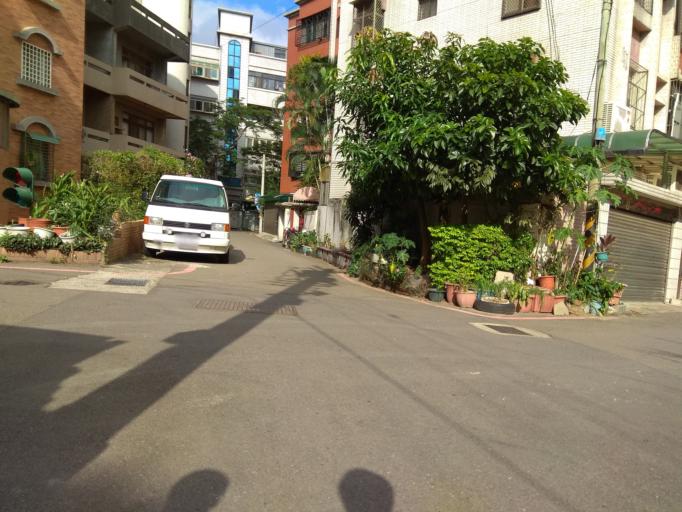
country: TW
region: Taiwan
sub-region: Hsinchu
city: Hsinchu
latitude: 24.7970
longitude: 120.9775
